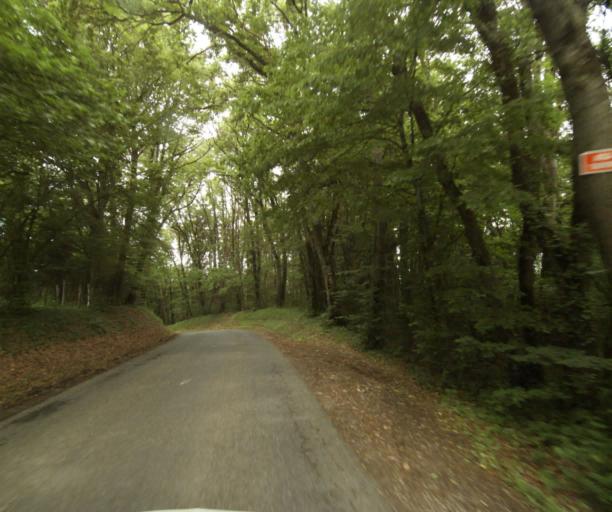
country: FR
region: Rhone-Alpes
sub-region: Departement de la Haute-Savoie
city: Allinges
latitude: 46.3449
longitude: 6.4555
